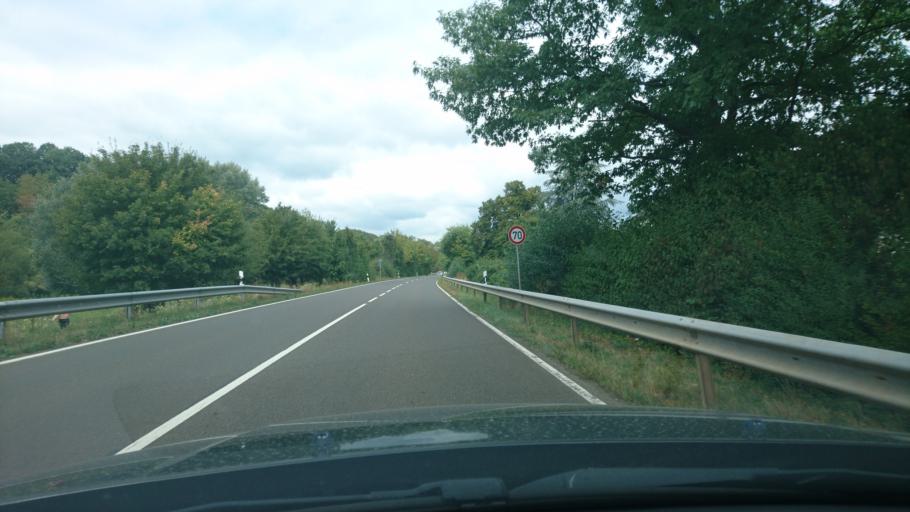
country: DE
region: Rheinland-Pfalz
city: Wiltingen
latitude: 49.6578
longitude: 6.5875
